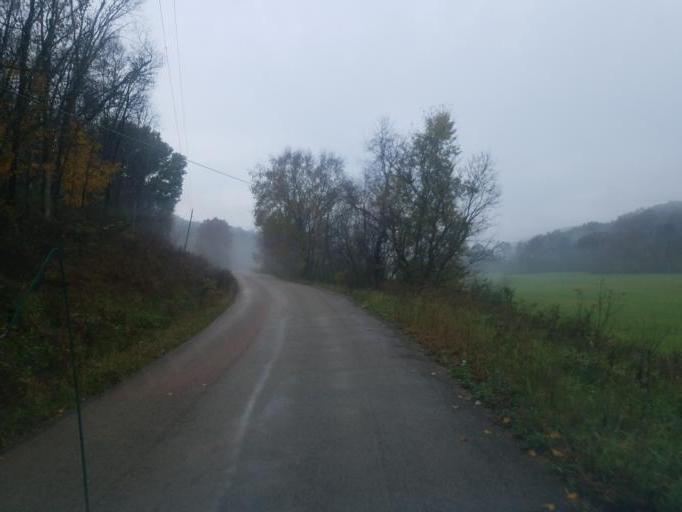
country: US
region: Ohio
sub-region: Athens County
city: Glouster
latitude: 39.4956
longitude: -81.9532
